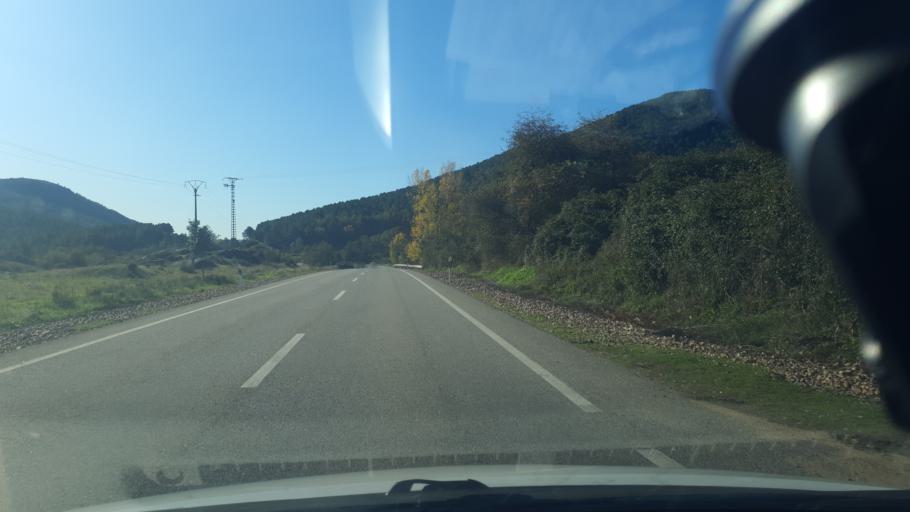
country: ES
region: Castille and Leon
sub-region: Provincia de Avila
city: Mombeltran
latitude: 40.2330
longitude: -5.0327
